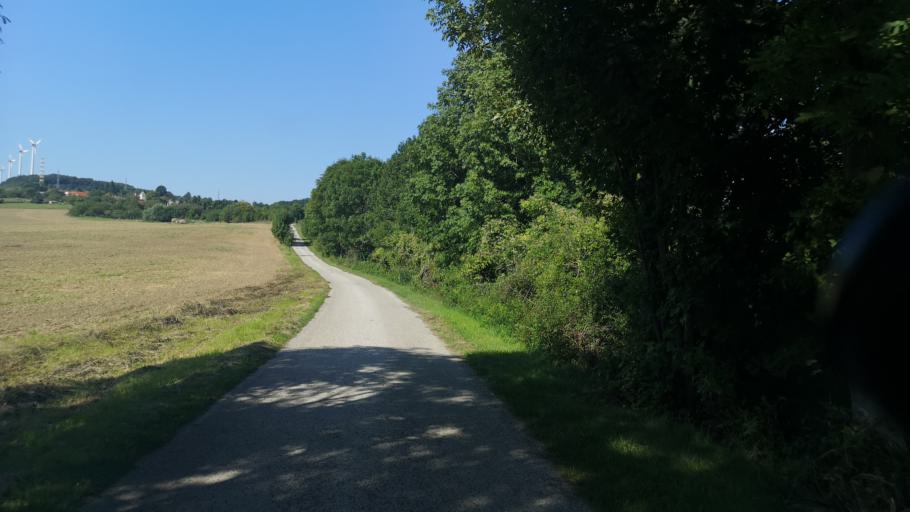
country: SK
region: Trnavsky
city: Smolenice
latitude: 48.5742
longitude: 17.4061
